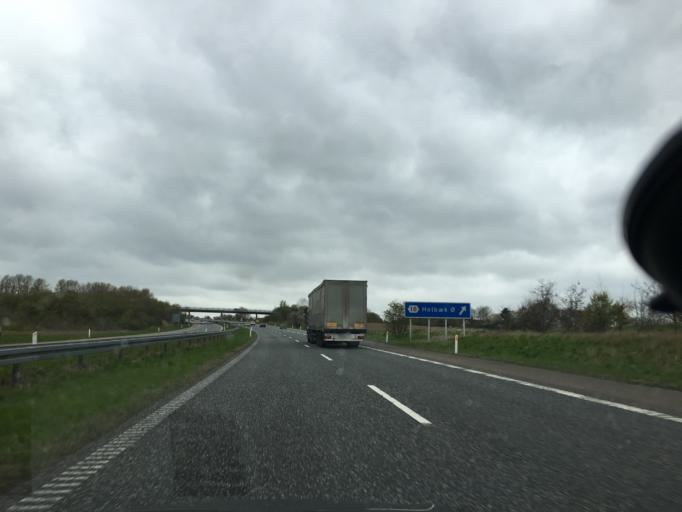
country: DK
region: Zealand
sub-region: Holbaek Kommune
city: Vipperod
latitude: 55.6758
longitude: 11.7451
